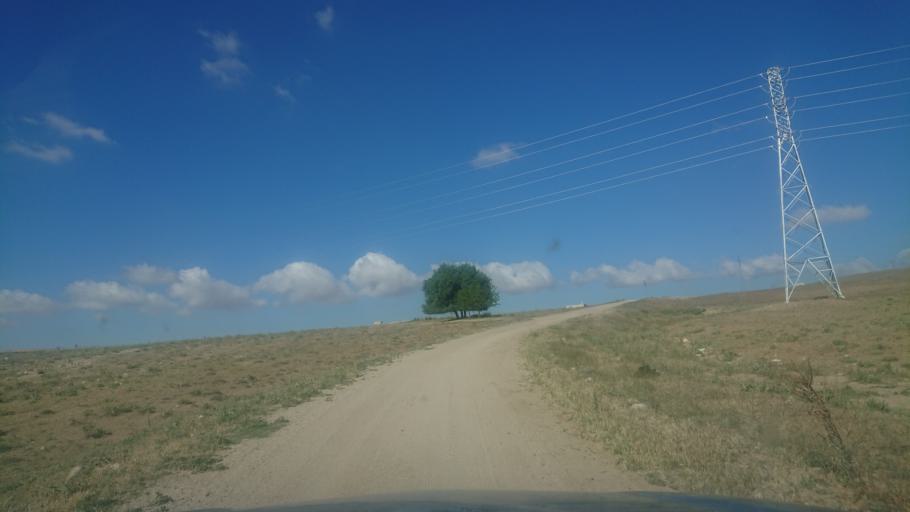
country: TR
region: Aksaray
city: Agacoren
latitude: 38.9186
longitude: 33.9222
